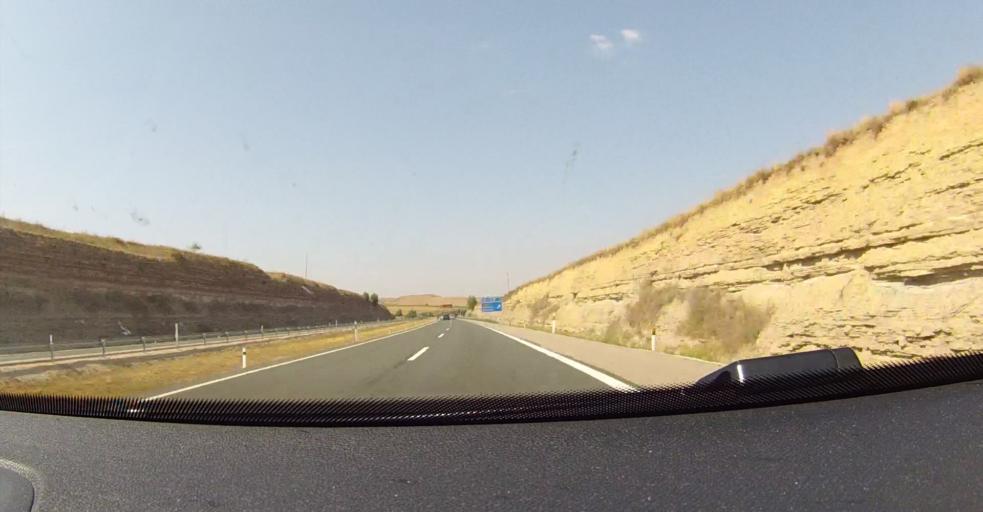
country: ES
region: Castille and Leon
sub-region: Provincia de Burgos
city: Briviesca
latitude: 42.5368
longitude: -3.3083
